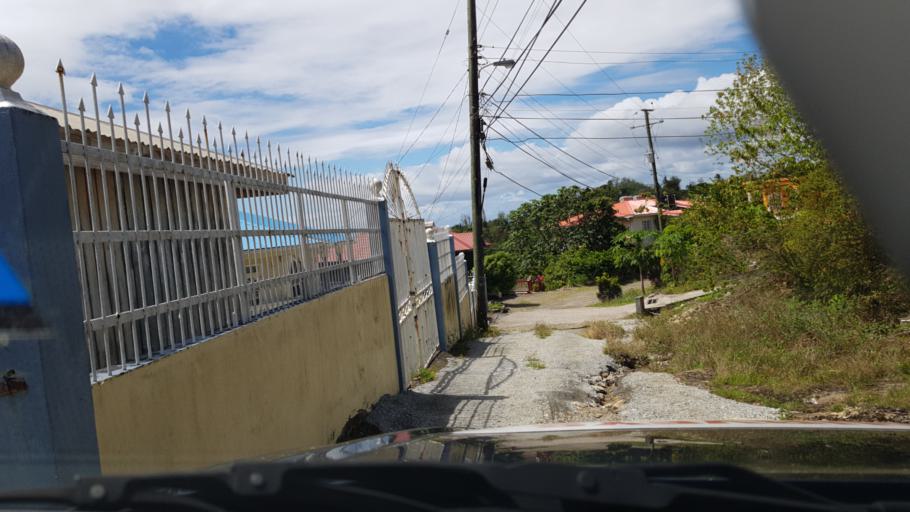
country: LC
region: Anse-la-Raye
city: Anse La Raye
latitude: 13.9462
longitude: -61.0381
